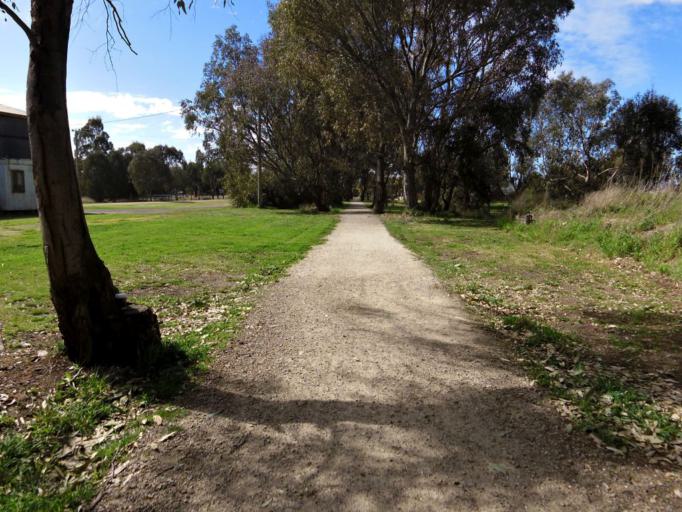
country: AU
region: Victoria
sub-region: Mansfield
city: Mansfield
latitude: -37.0503
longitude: 146.0809
